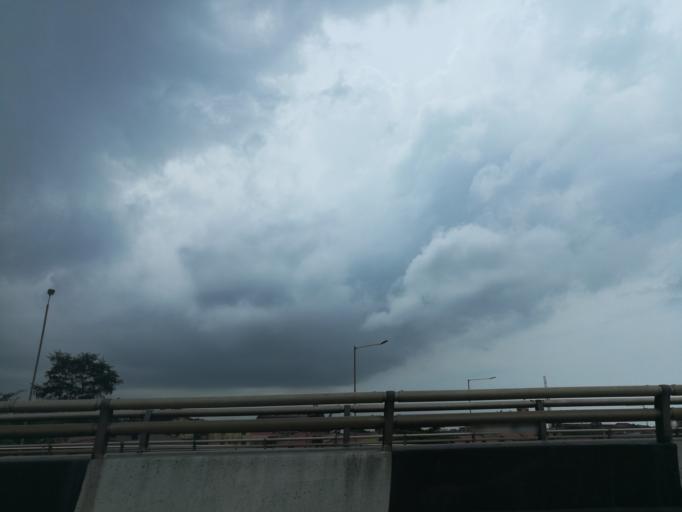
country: NG
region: Lagos
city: Lagos
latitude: 6.4513
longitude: 3.4083
